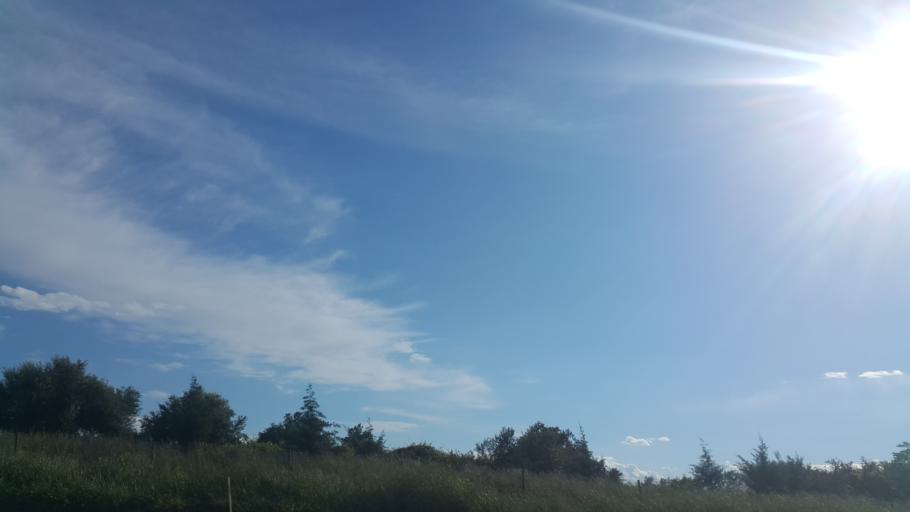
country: TR
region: Adana
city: Yakapinar
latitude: 37.0127
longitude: 35.5051
